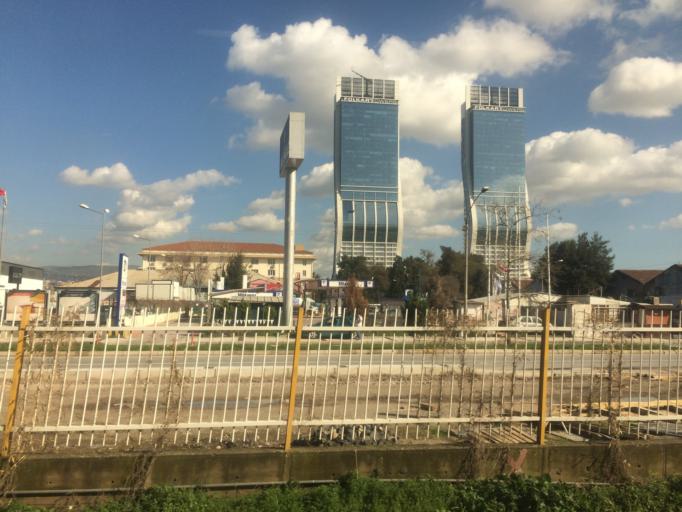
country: TR
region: Izmir
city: Izmir
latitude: 38.4535
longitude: 27.1712
